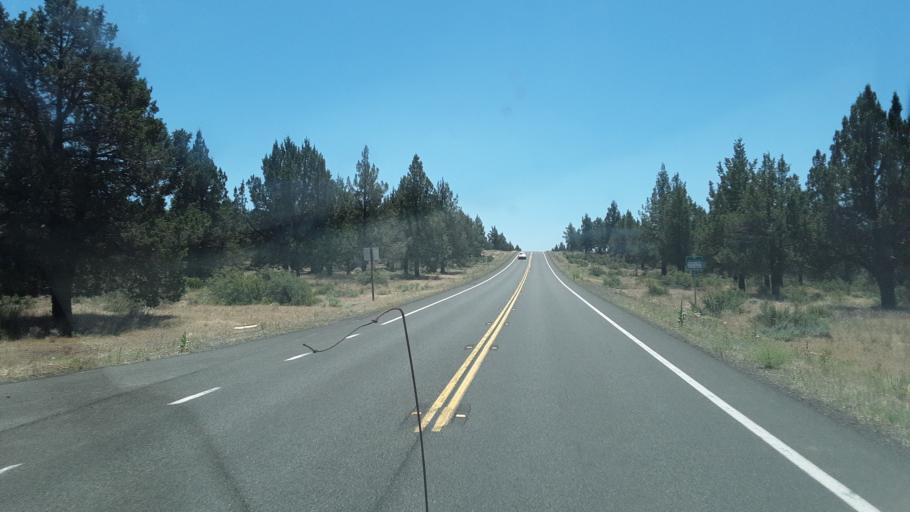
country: US
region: California
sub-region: Siskiyou County
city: Tulelake
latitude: 41.6521
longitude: -121.2432
